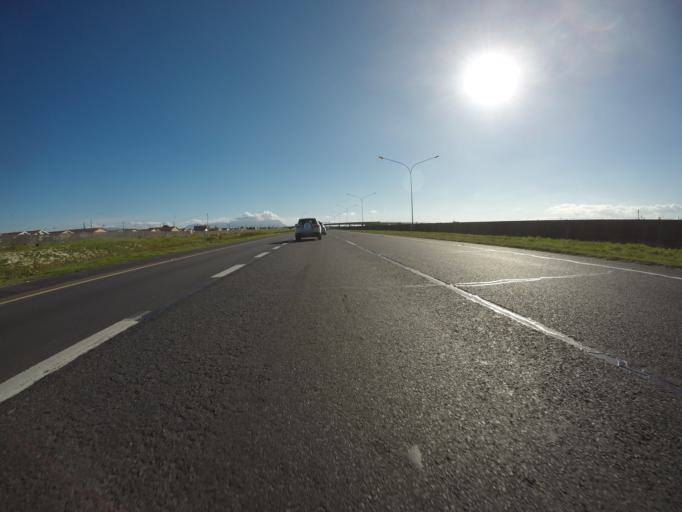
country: ZA
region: Western Cape
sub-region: City of Cape Town
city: Lansdowne
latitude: -34.0058
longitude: 18.6439
